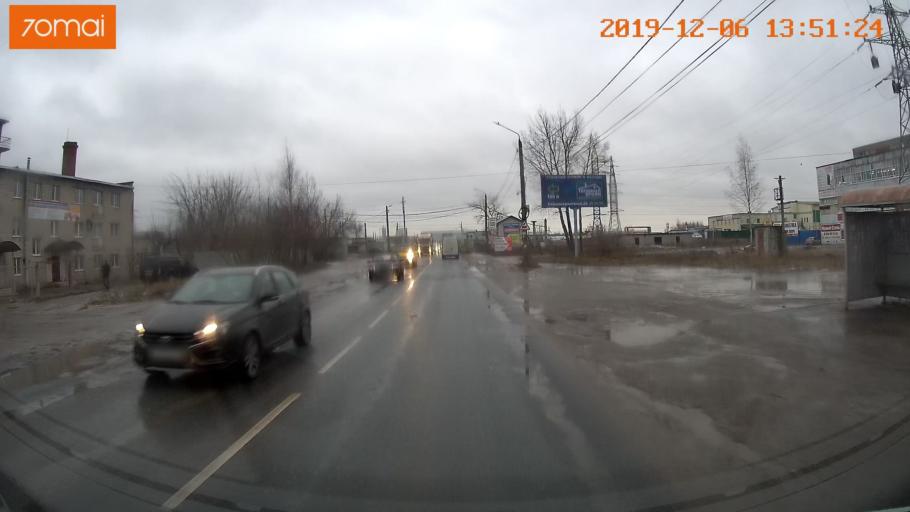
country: RU
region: Ivanovo
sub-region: Gorod Ivanovo
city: Ivanovo
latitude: 56.9682
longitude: 40.9524
